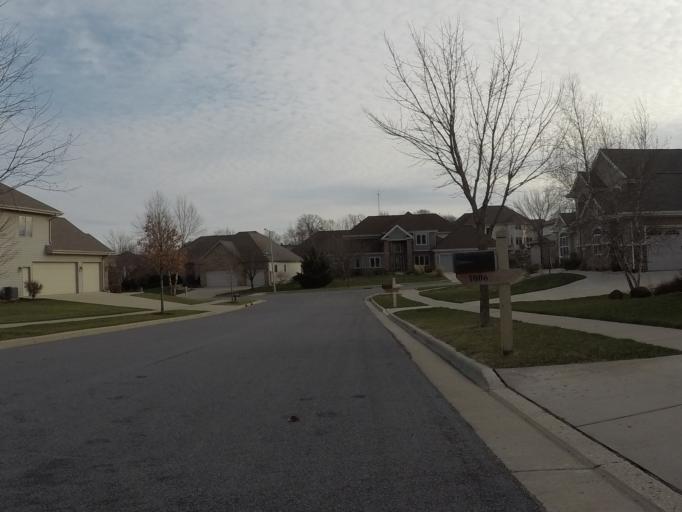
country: US
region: Wisconsin
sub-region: Dane County
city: Middleton
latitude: 43.0798
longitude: -89.5583
